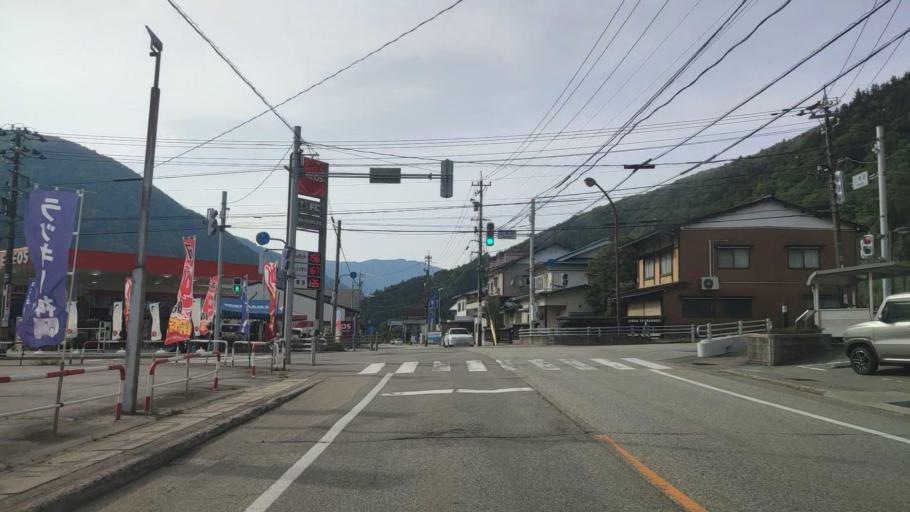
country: JP
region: Gifu
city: Takayama
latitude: 36.3271
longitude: 137.3078
